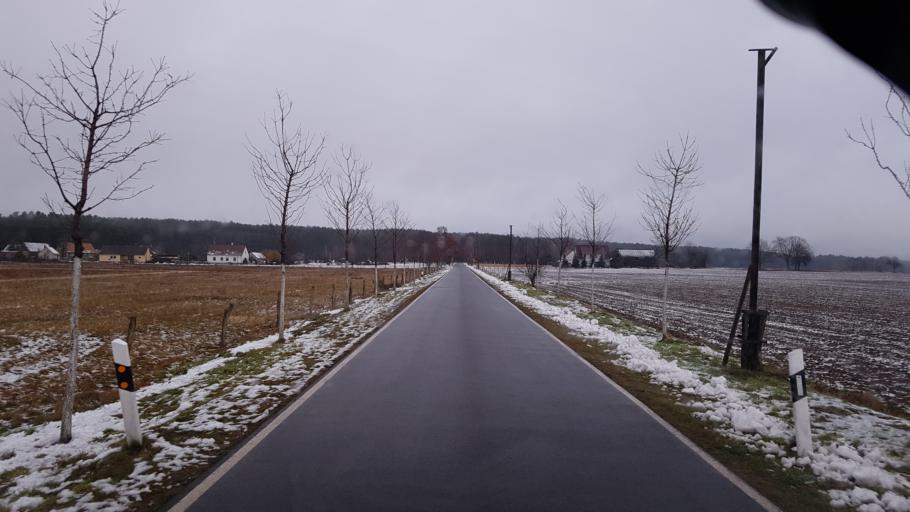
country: DE
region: Brandenburg
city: Neu Zauche
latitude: 51.9460
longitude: 14.1151
